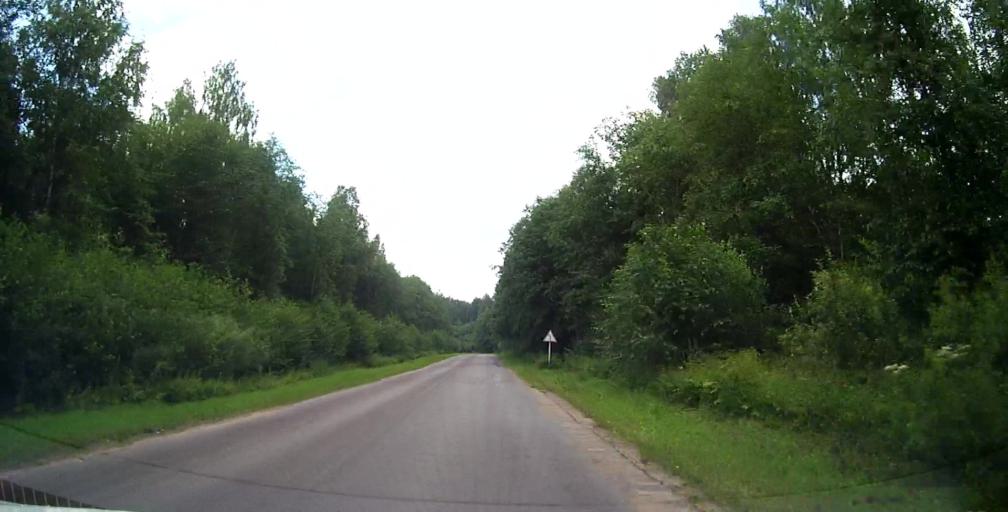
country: RU
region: Smolensk
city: Demidov
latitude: 55.4739
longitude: 31.6339
